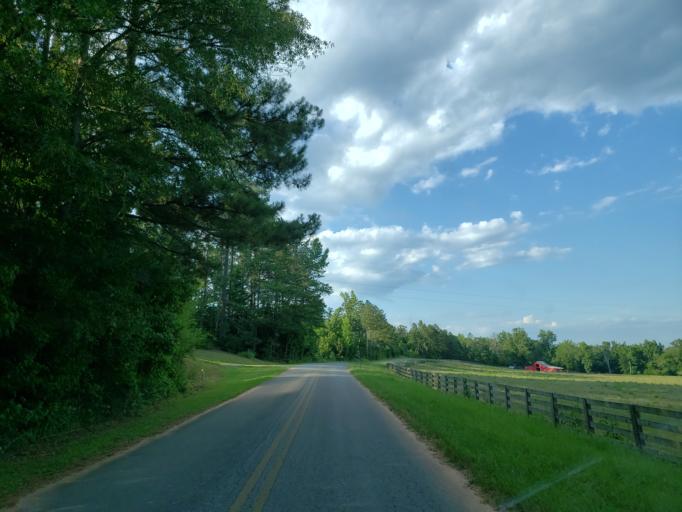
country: US
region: Georgia
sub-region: Haralson County
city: Tallapoosa
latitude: 33.8222
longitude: -85.2837
